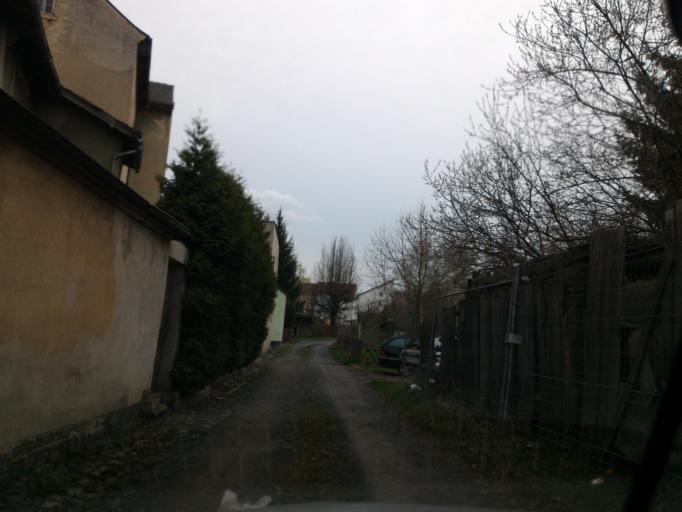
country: DE
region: Saxony
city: Zittau
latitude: 50.8862
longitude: 14.8150
